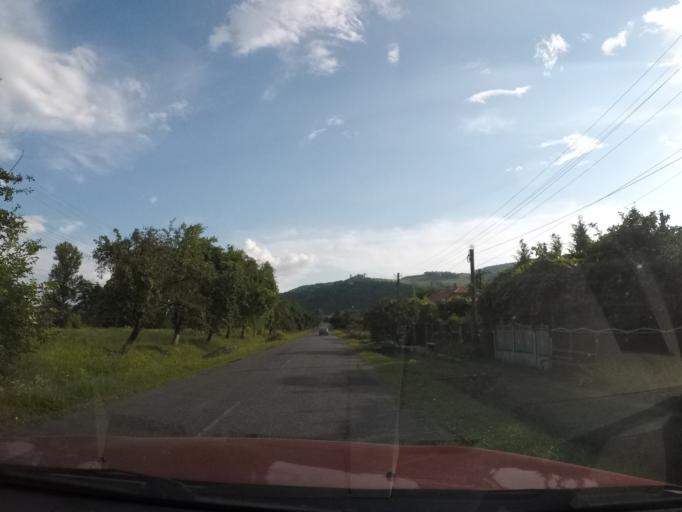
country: UA
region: Zakarpattia
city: Velykyi Bereznyi
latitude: 48.9312
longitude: 22.4600
